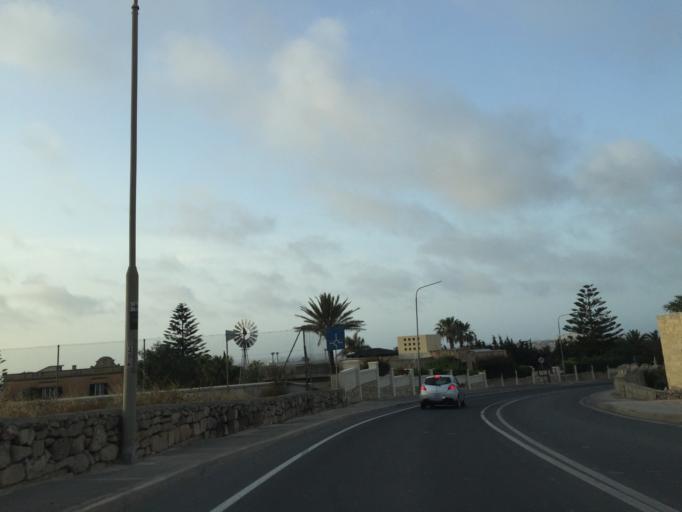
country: MT
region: Il-Mosta
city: Mosta
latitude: 35.9152
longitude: 14.4157
